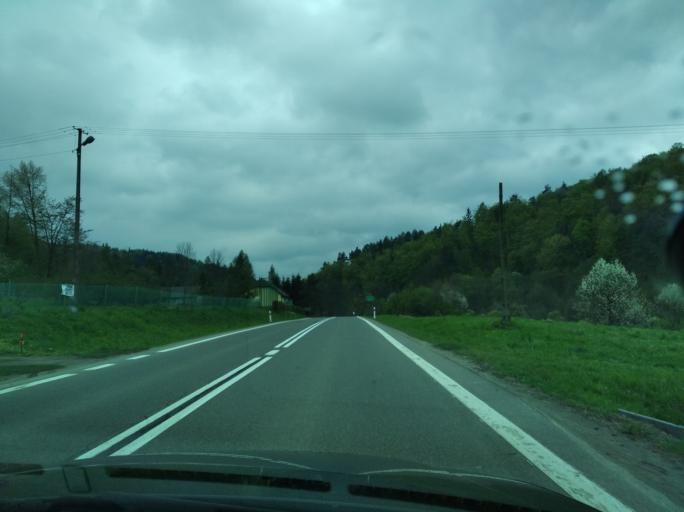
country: PL
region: Subcarpathian Voivodeship
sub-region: Powiat sanocki
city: Zagorz
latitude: 49.5429
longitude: 22.3022
